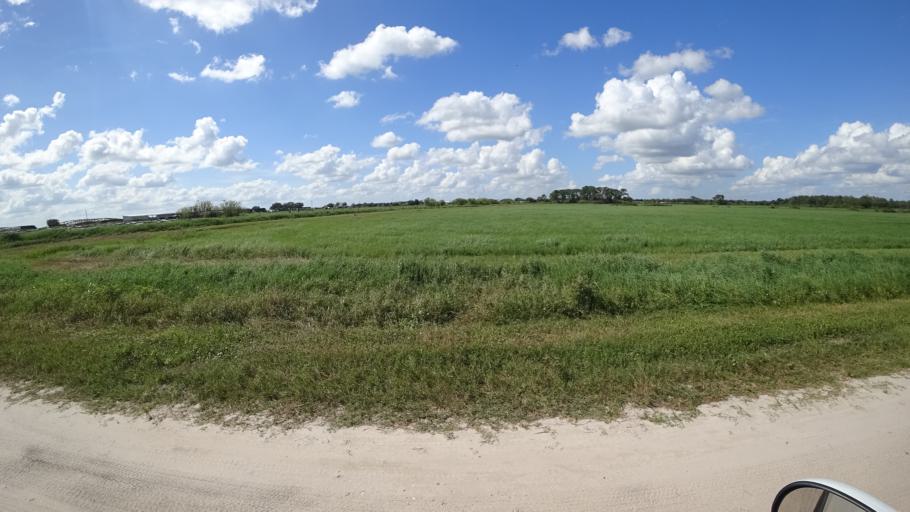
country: US
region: Florida
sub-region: DeSoto County
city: Arcadia
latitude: 27.3150
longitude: -82.1252
